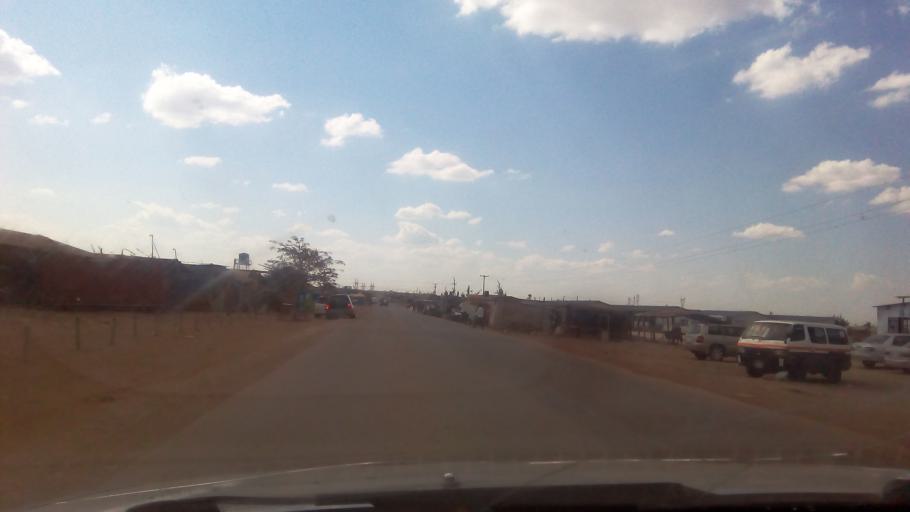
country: ZM
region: Lusaka
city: Lusaka
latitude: -15.4676
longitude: 28.3421
